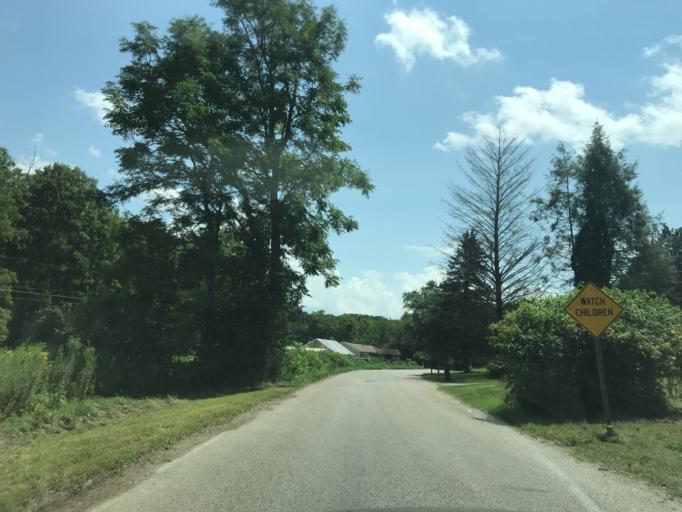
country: US
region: Pennsylvania
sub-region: York County
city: New Freedom
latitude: 39.7237
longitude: -76.7200
